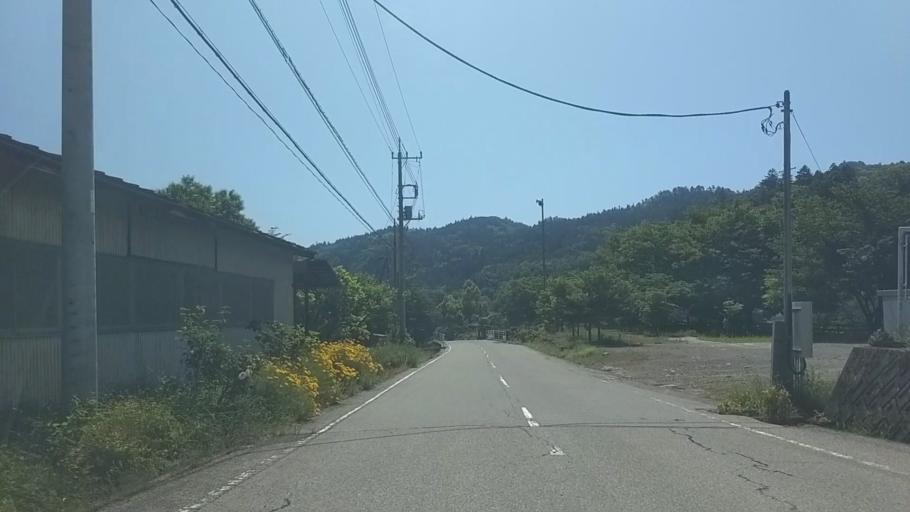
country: JP
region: Yamanashi
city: Ryuo
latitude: 35.5073
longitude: 138.4236
